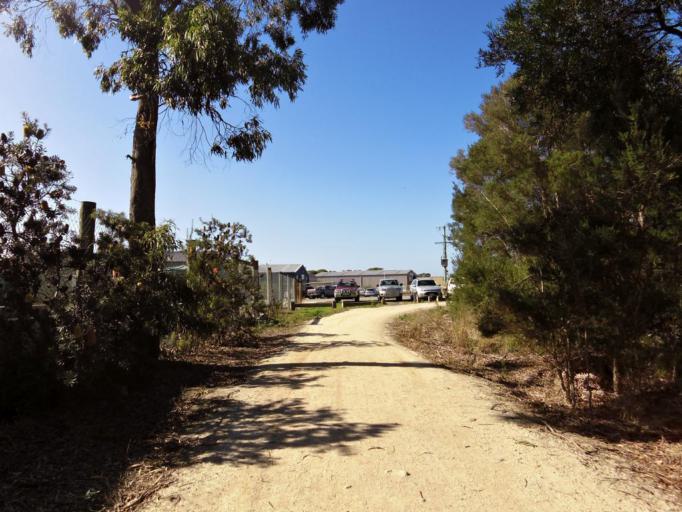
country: AU
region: Victoria
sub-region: Bass Coast
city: North Wonthaggi
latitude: -38.6074
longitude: 145.6027
